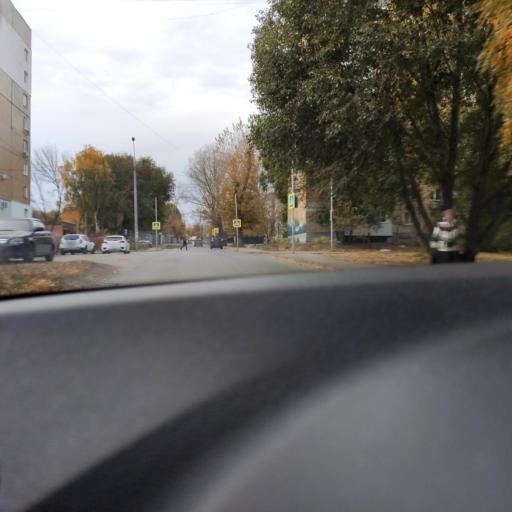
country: RU
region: Samara
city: Samara
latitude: 53.2373
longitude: 50.2528
